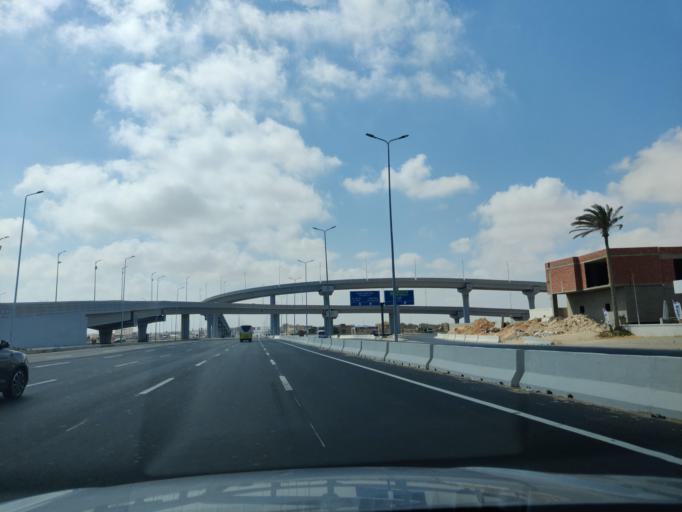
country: EG
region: Muhafazat Matruh
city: Al `Alamayn
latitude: 30.9530
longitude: 28.7696
